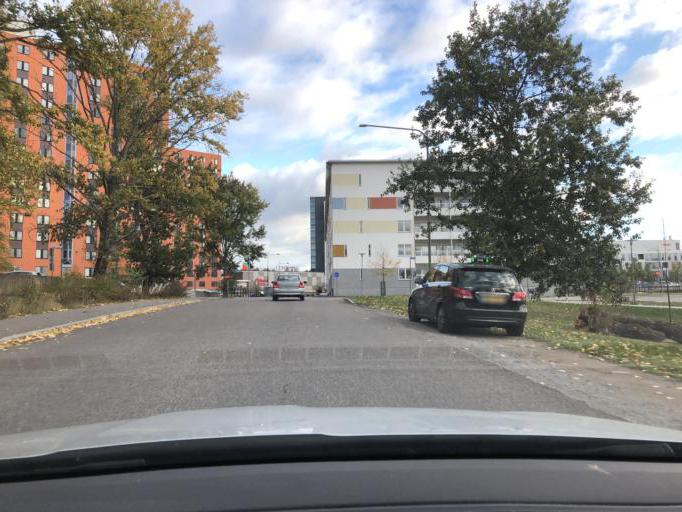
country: SE
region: Stockholm
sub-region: Botkyrka Kommun
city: Tullinge
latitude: 59.2240
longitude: 17.9355
